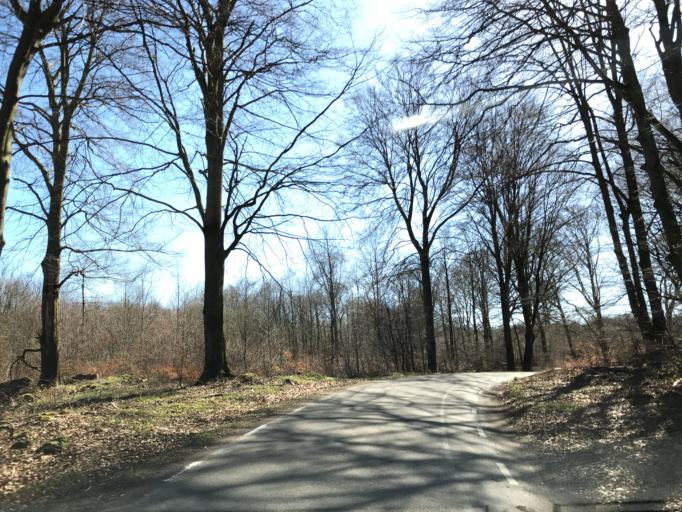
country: SE
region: Skane
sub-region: Svalovs Kommun
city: Kagerod
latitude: 56.0330
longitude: 13.1599
